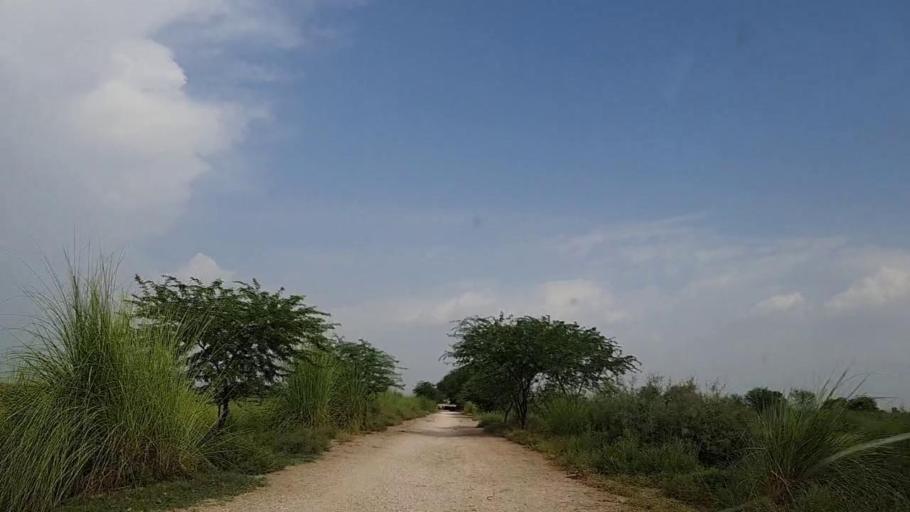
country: PK
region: Sindh
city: Khanpur
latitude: 27.8259
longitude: 69.5168
